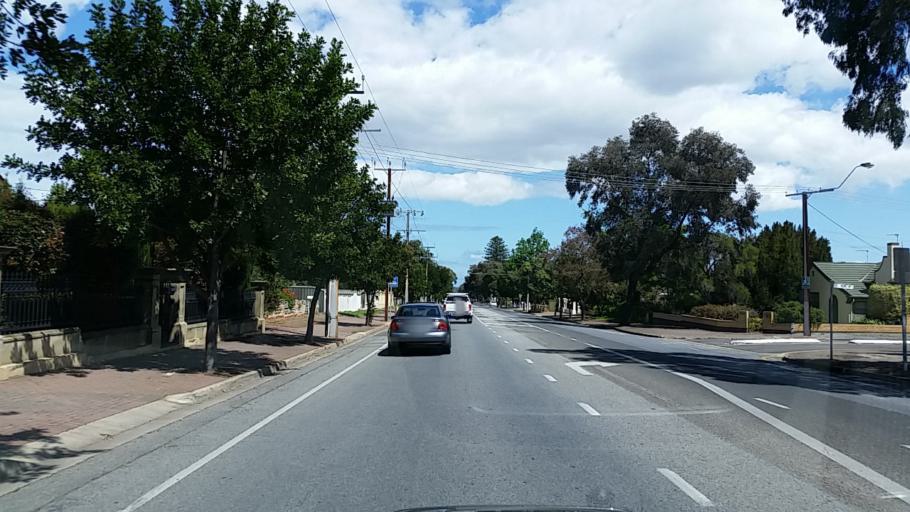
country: AU
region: South Australia
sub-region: Burnside
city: Kensington Gardens
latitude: -34.9136
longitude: 138.6655
